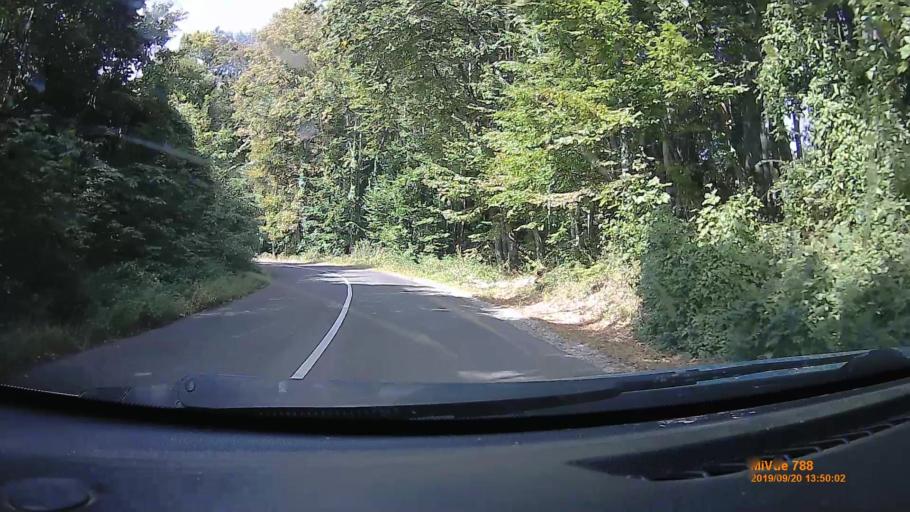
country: HU
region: Borsod-Abauj-Zemplen
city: Saly
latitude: 48.0667
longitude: 20.5914
